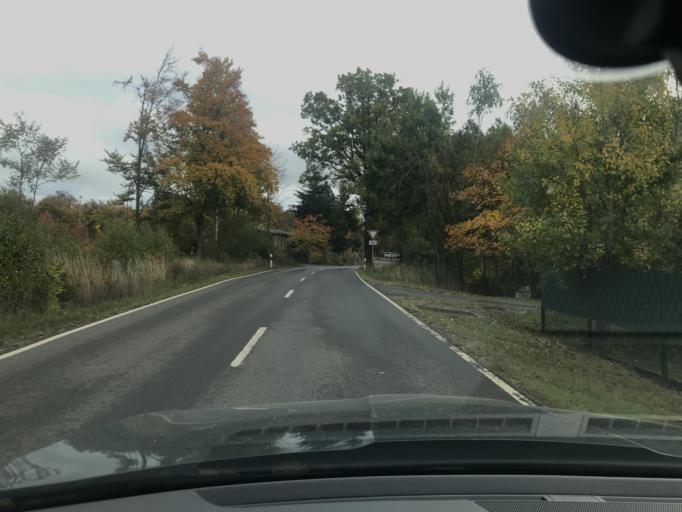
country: DE
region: Saxony-Anhalt
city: Friedrichsbrunn
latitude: 51.6949
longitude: 11.0487
